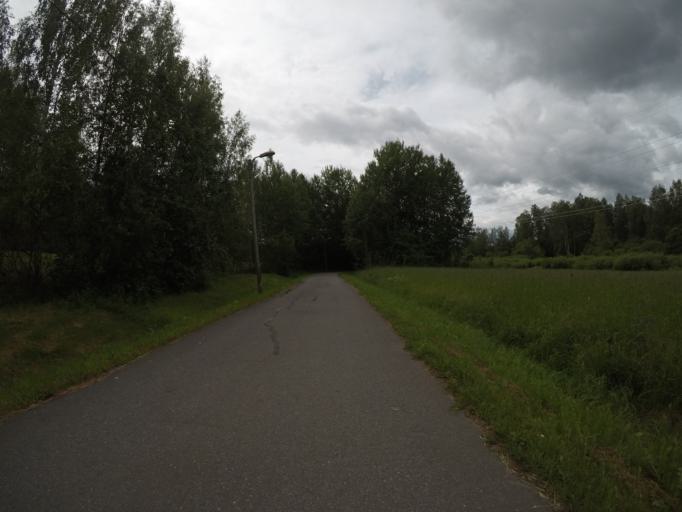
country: FI
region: Haeme
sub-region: Haemeenlinna
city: Haemeenlinna
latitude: 60.9972
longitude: 24.4956
